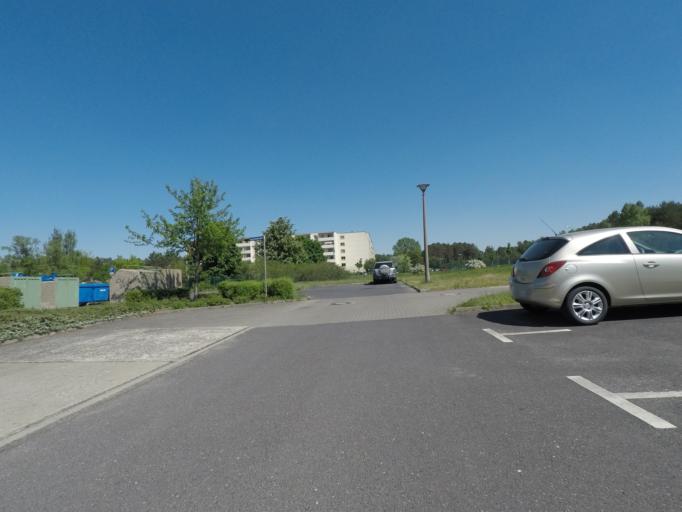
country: DE
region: Brandenburg
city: Eberswalde
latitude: 52.8298
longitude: 13.7533
